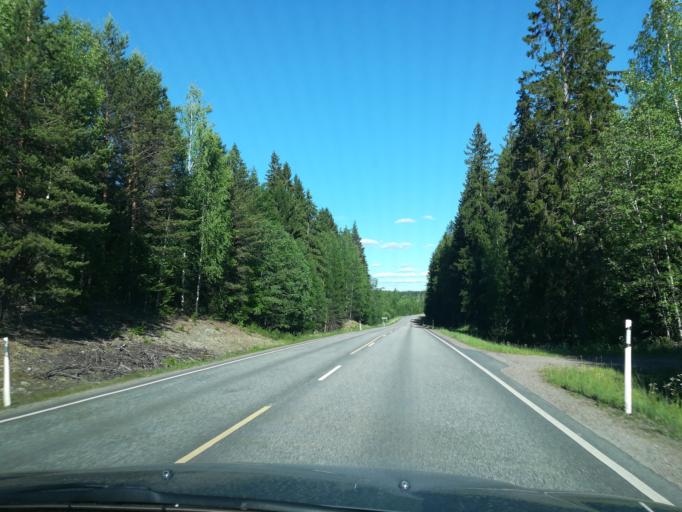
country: FI
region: South Karelia
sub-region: Imatra
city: Ruokolahti
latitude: 61.3510
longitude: 28.7419
